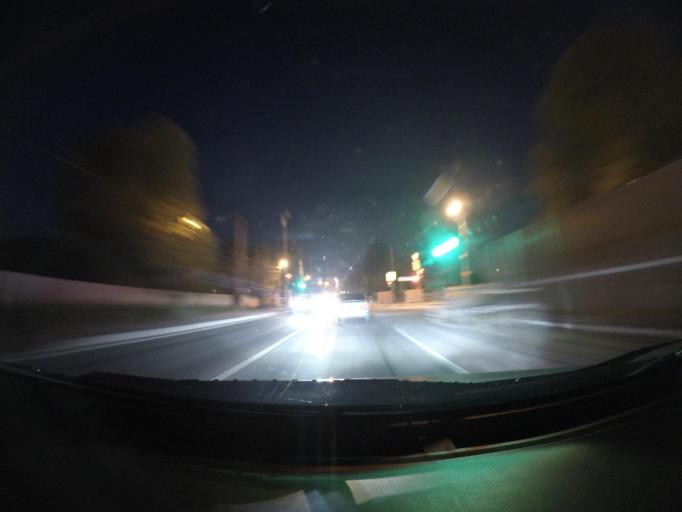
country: RU
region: Moskovskaya
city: Novopodrezkovo
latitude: 55.9213
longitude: 37.3774
